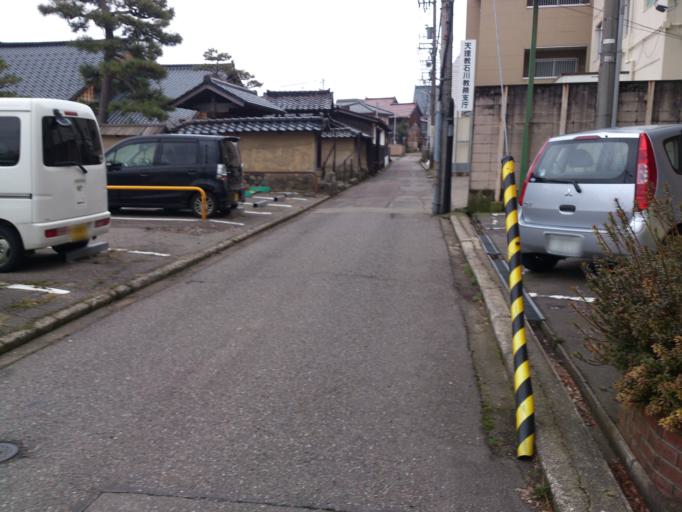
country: JP
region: Ishikawa
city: Kanazawa-shi
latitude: 36.5696
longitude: 136.6457
